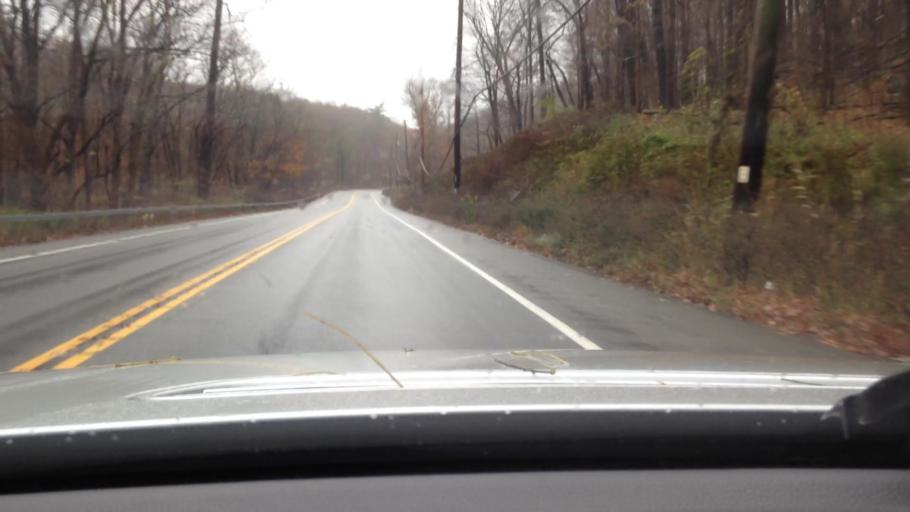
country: US
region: New York
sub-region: Westchester County
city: Peekskill
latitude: 41.3314
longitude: -73.9252
